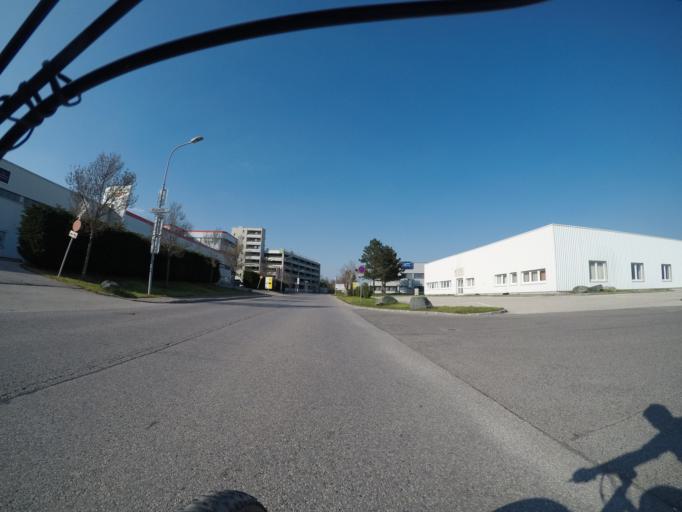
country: AT
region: Lower Austria
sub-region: Politischer Bezirk Modling
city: Neu-Guntramsdorf
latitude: 48.0725
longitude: 16.3156
